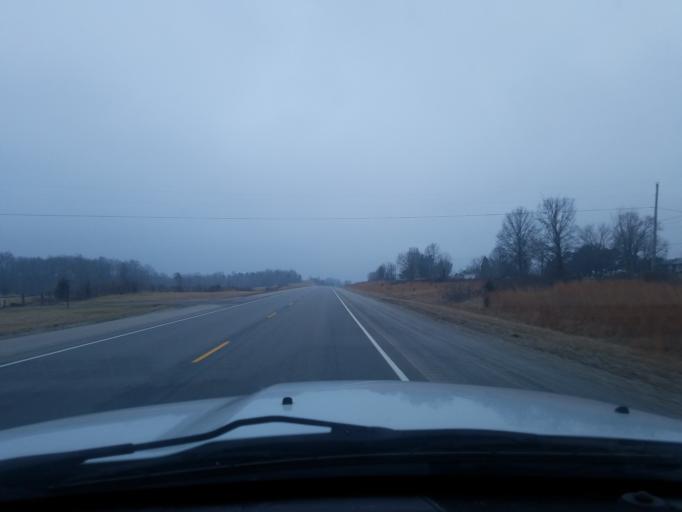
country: US
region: Indiana
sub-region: Crawford County
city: English
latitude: 38.2145
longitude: -86.5930
